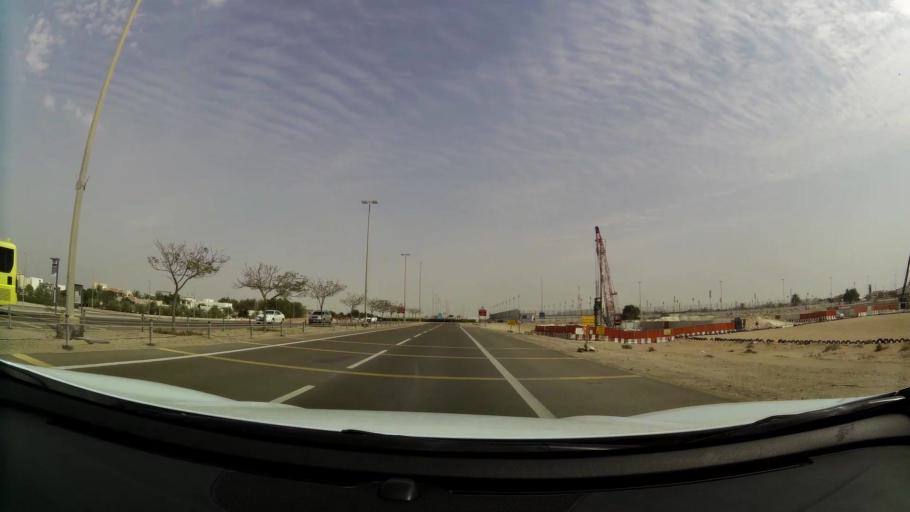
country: AE
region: Abu Dhabi
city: Abu Dhabi
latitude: 24.5651
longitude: 54.6849
